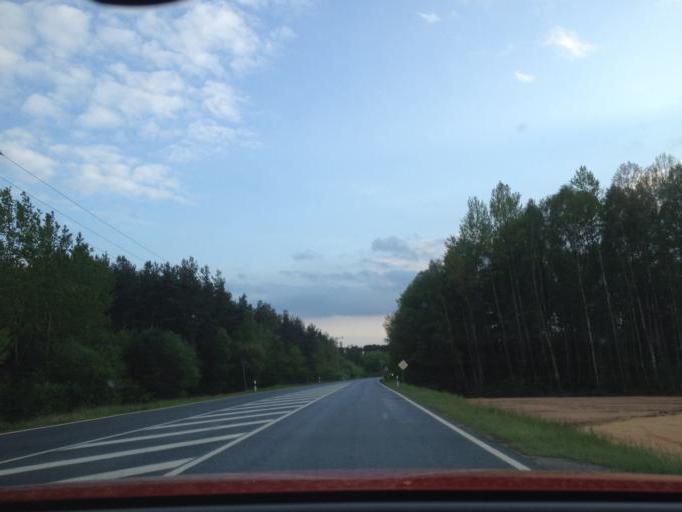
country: DE
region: Bavaria
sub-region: Upper Palatinate
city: Etzenricht
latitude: 49.6231
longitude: 12.0954
